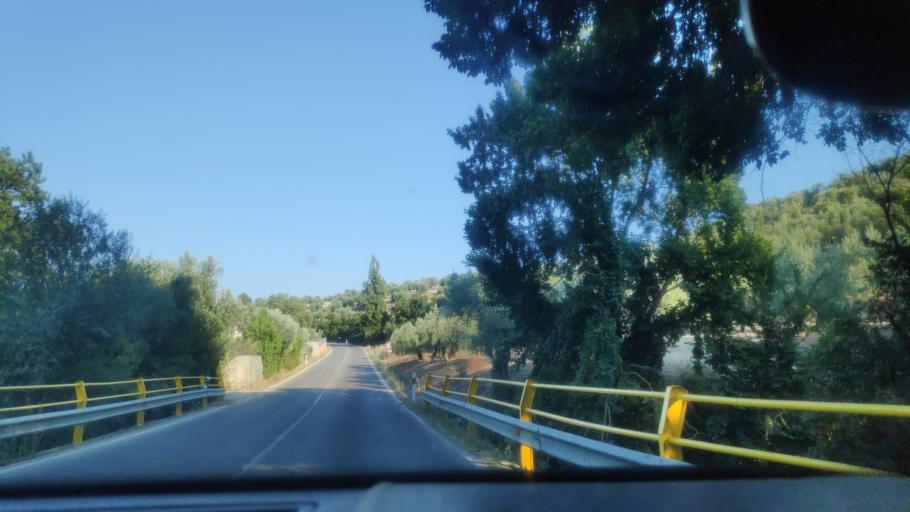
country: ES
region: Andalusia
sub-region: Provincia de Jaen
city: Jaen
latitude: 37.7492
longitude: -3.7941
